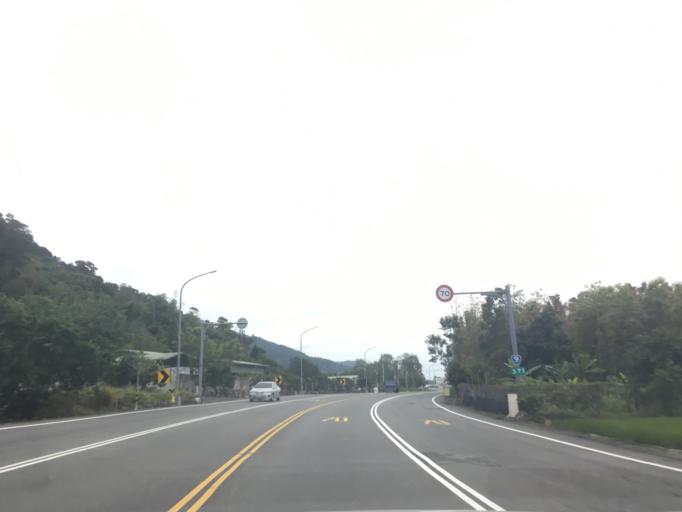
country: TW
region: Taiwan
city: Taitung City
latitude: 22.7391
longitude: 121.0566
